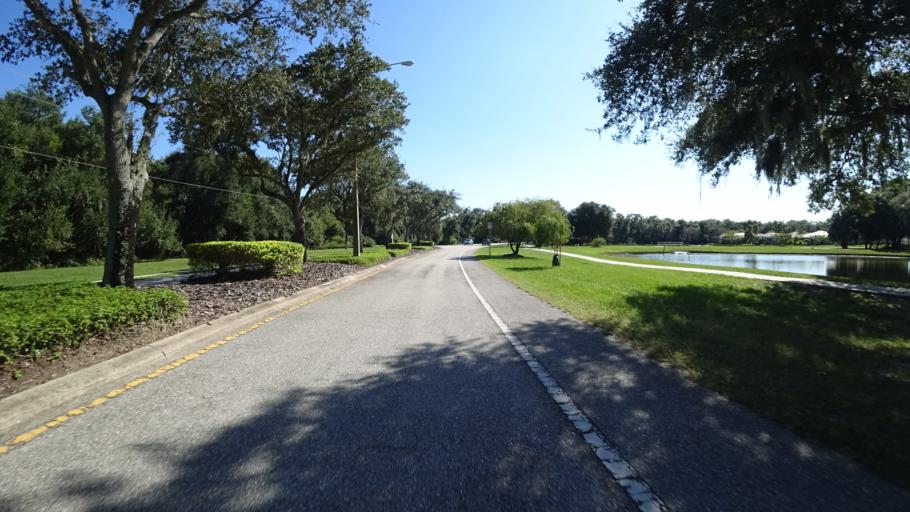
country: US
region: Florida
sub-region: Sarasota County
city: The Meadows
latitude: 27.4227
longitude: -82.4328
